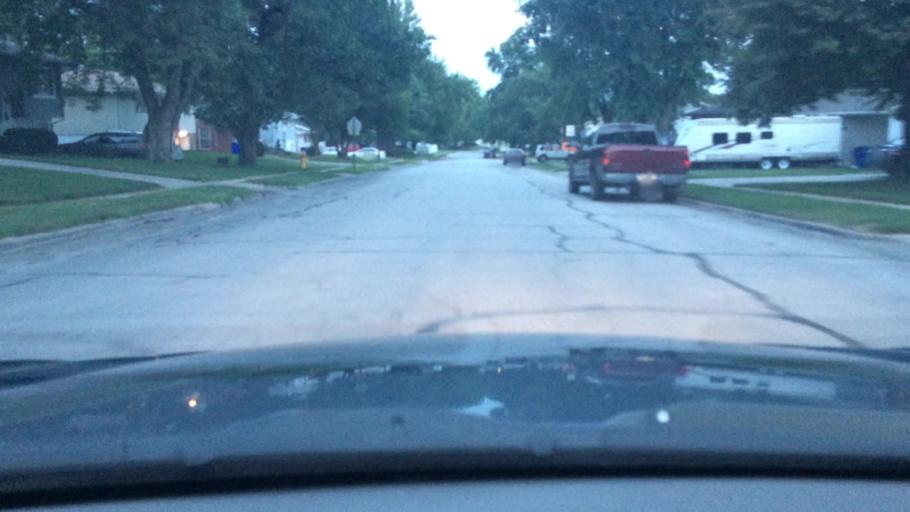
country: US
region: Nebraska
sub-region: Sarpy County
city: La Vista
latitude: 41.1857
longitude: -96.0379
